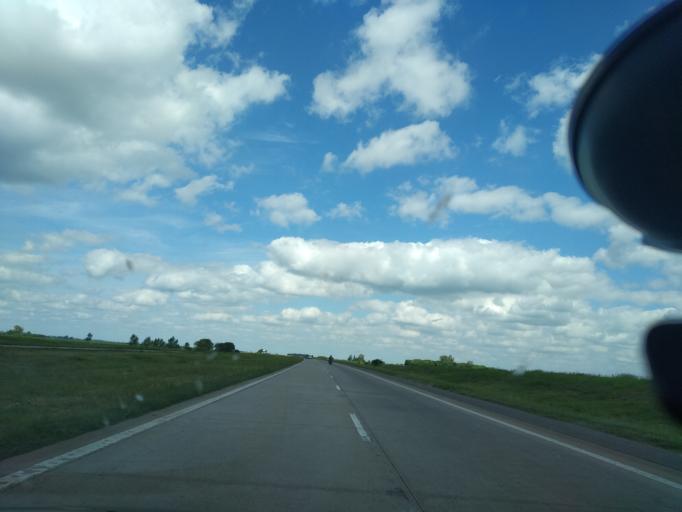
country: AR
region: Santa Fe
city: Canada de Gomez
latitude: -32.8363
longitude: -61.4585
